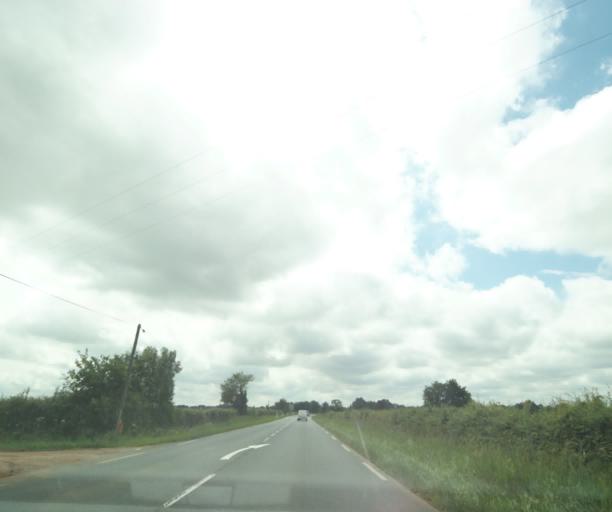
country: FR
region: Poitou-Charentes
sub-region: Departement des Deux-Sevres
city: Viennay
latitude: 46.7060
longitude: -0.2391
